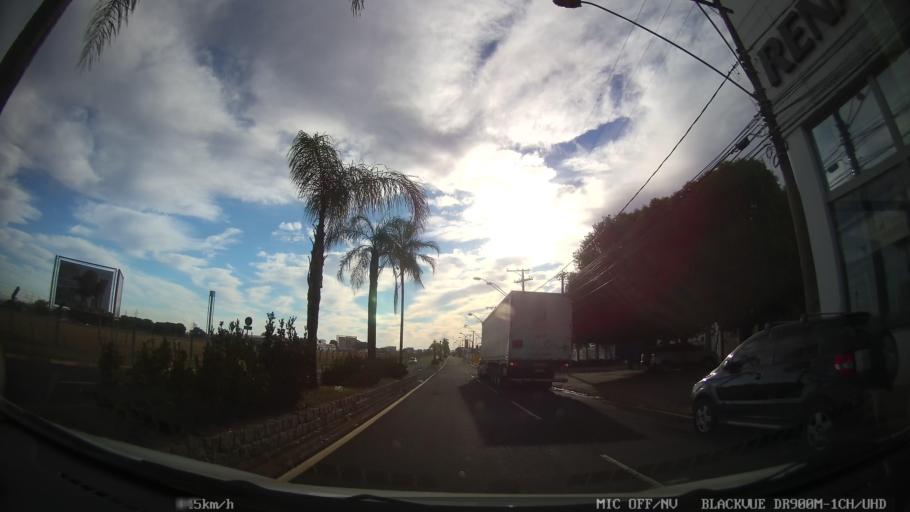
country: BR
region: Sao Paulo
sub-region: Catanduva
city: Catanduva
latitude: -21.1489
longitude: -48.9876
